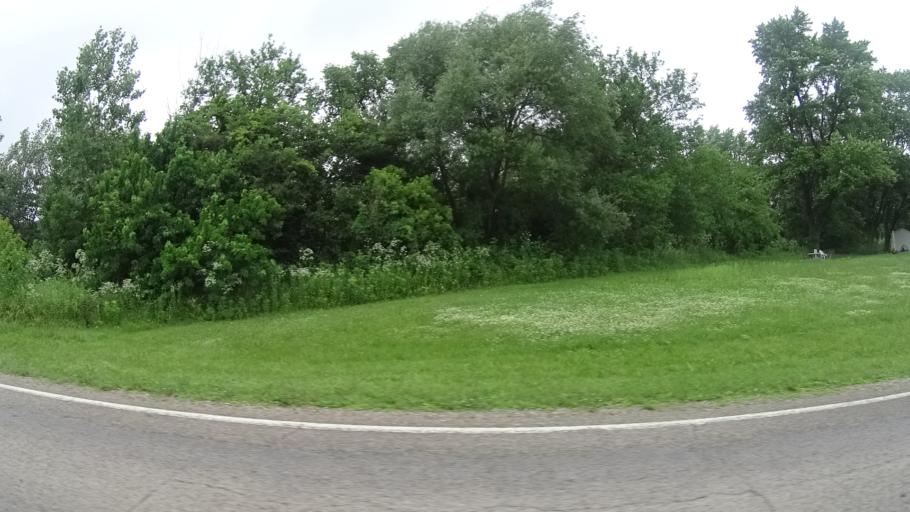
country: US
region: Ohio
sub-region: Huron County
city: Bellevue
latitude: 41.3419
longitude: -82.8088
